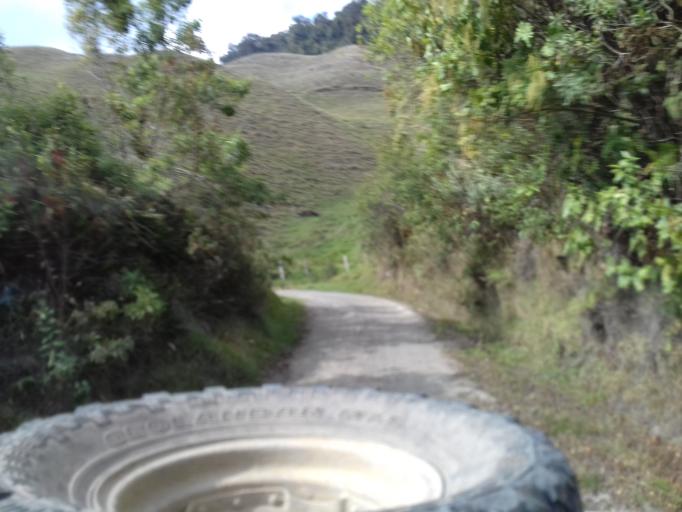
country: CO
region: Quindio
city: Salento
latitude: 4.5471
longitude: -75.4904
